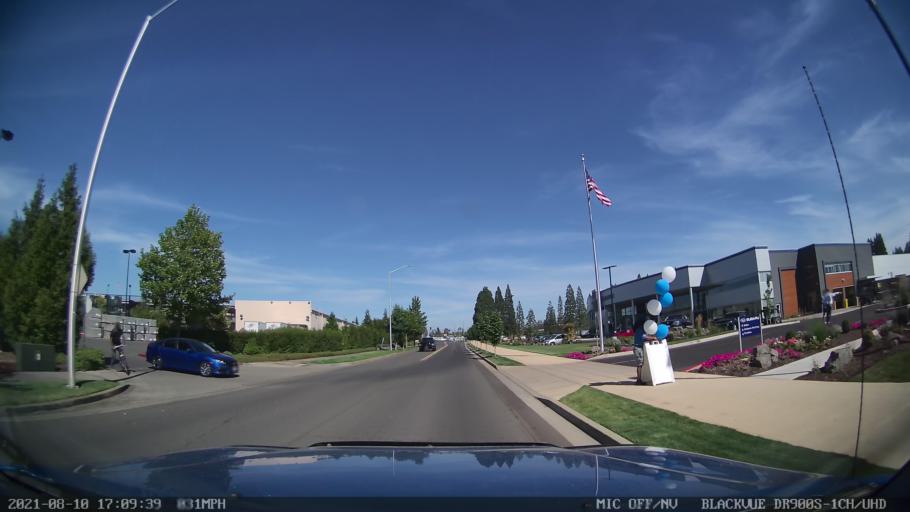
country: US
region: Oregon
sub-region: Marion County
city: Keizer
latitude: 44.9697
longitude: -123.0231
